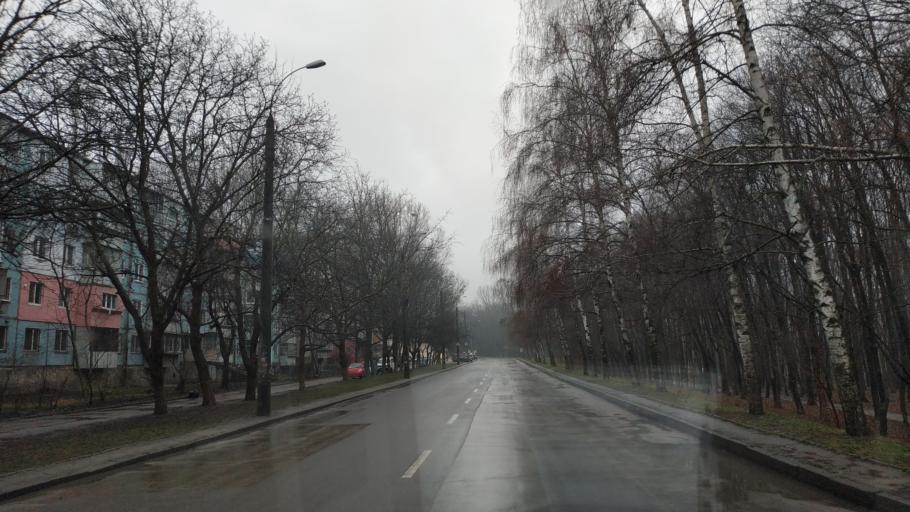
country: MD
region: Chisinau
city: Vatra
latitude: 47.0381
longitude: 28.7822
